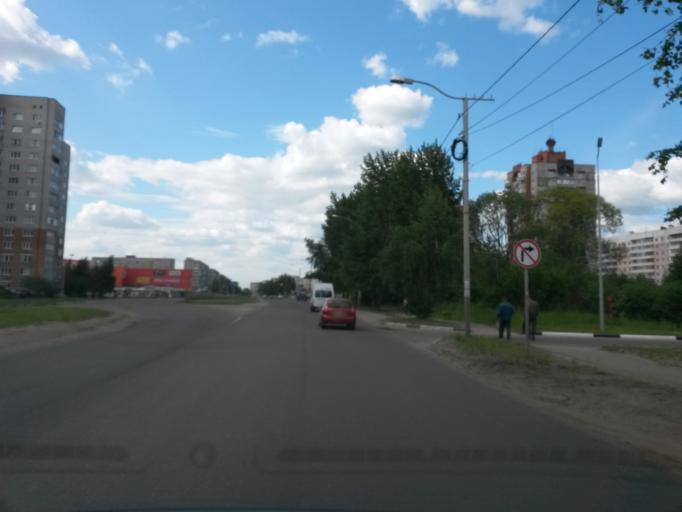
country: RU
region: Jaroslavl
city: Yaroslavl
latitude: 57.6435
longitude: 39.9575
